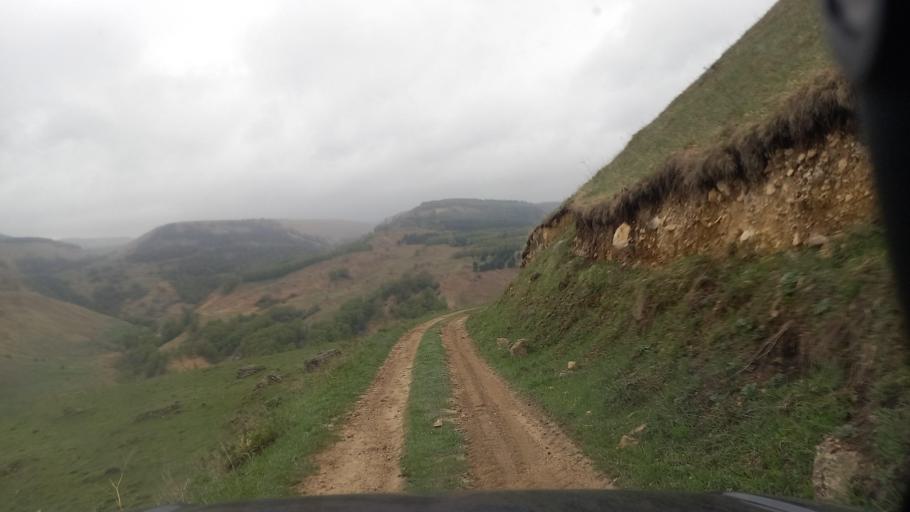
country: RU
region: Stavropol'skiy
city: Nezhinskiy
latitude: 43.8517
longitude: 42.6386
